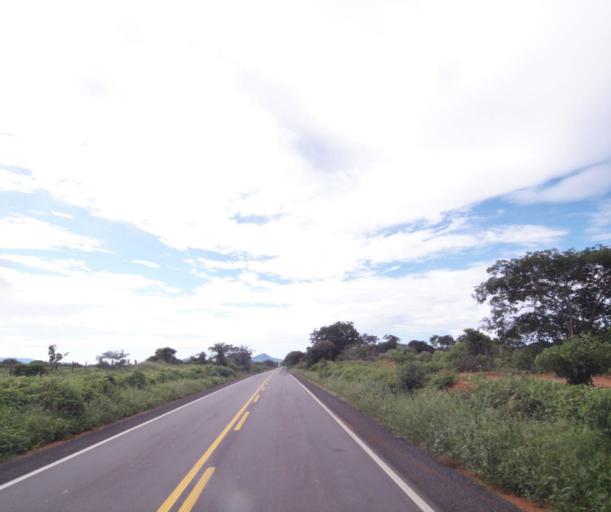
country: BR
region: Bahia
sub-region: Guanambi
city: Guanambi
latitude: -14.4060
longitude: -42.7442
